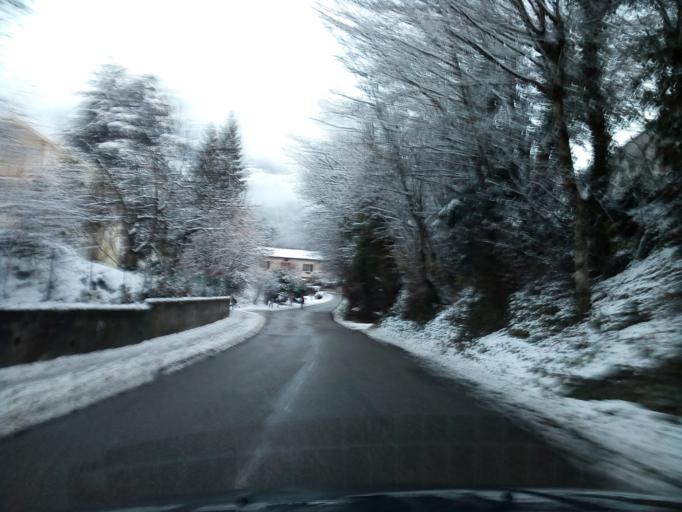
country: FR
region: Rhone-Alpes
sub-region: Departement de l'Isere
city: Corenc
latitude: 45.2187
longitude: 5.7791
